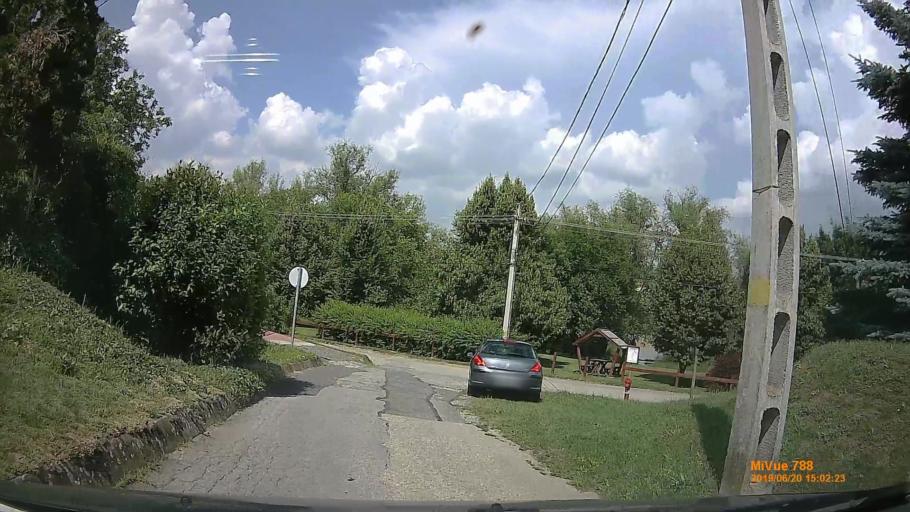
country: HU
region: Baranya
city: Kozarmisleny
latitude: 45.9846
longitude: 18.2627
